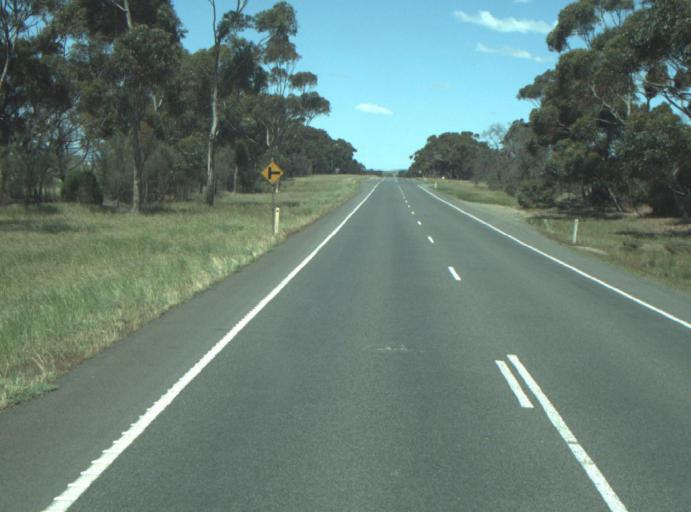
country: AU
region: Victoria
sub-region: Greater Geelong
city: Lara
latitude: -37.9574
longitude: 144.3517
